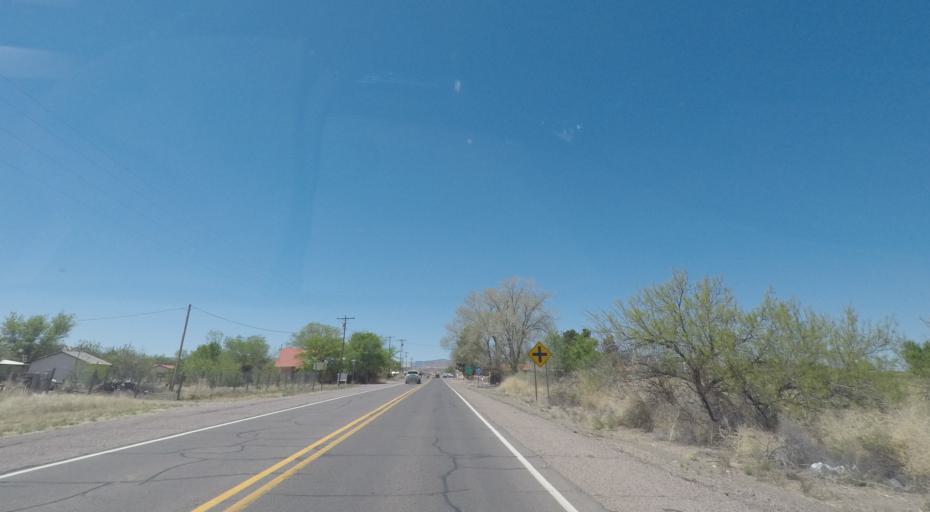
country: US
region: New Mexico
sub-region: Socorro County
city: Socorro
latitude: 33.9180
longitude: -106.8652
